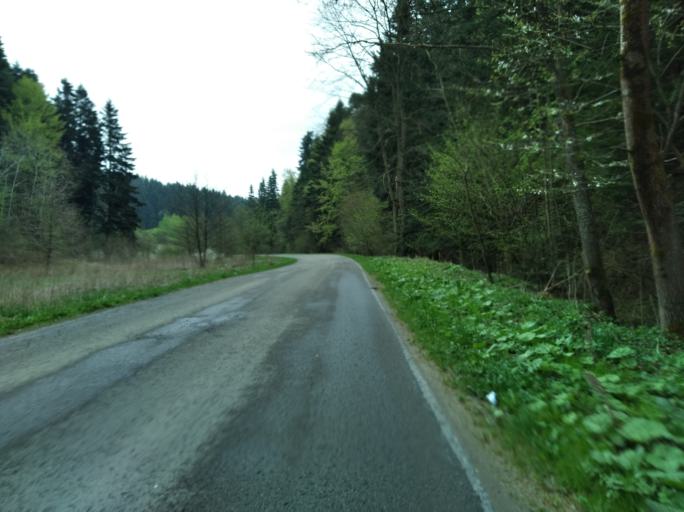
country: PL
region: Subcarpathian Voivodeship
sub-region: Powiat brzozowski
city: Golcowa
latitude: 49.7498
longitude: 22.0702
